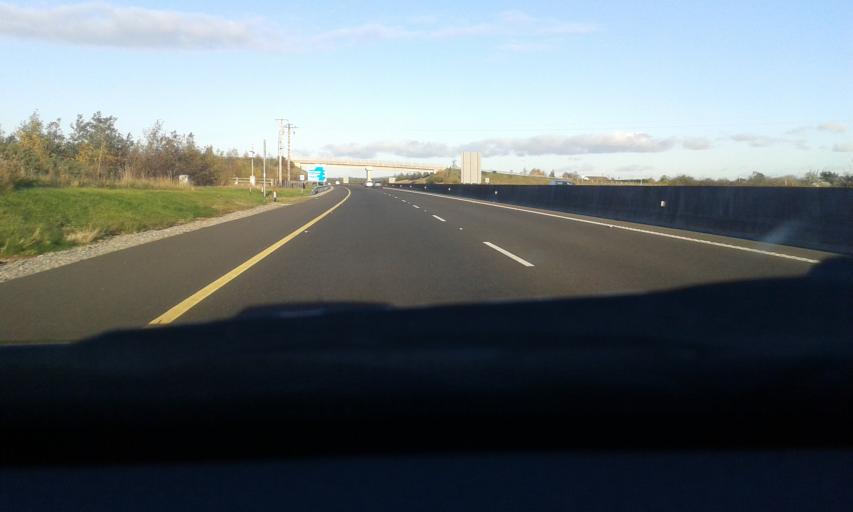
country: IE
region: Munster
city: Thurles
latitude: 52.6698
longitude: -7.6956
